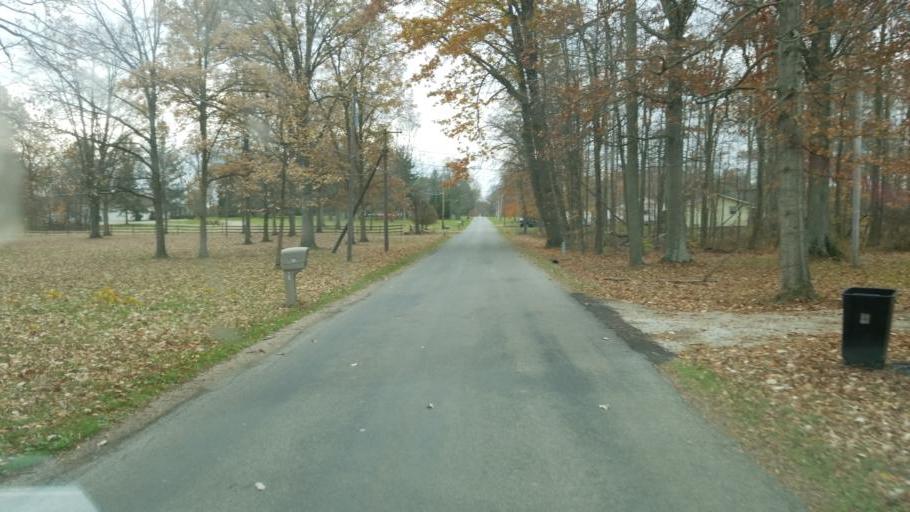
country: US
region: Ohio
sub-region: Crawford County
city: Crestline
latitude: 40.7403
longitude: -82.6889
